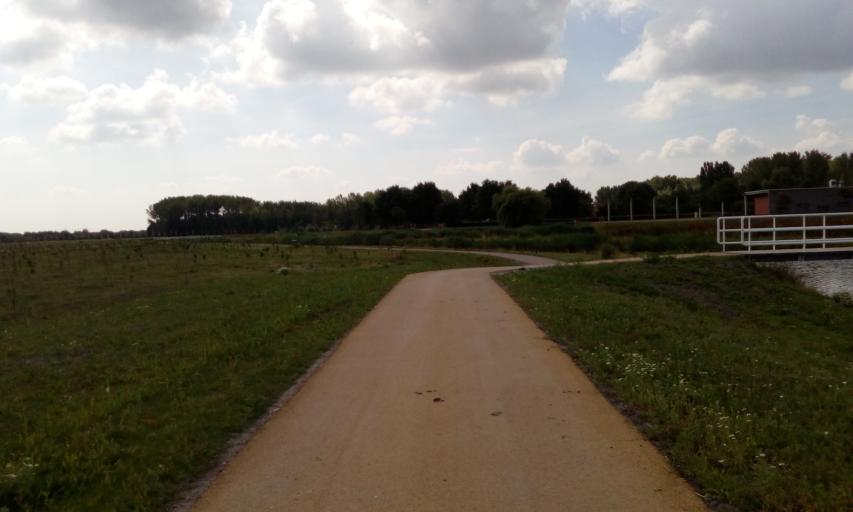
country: NL
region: South Holland
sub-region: Gemeente Pijnacker-Nootdorp
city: Pijnacker
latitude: 52.0371
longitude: 4.4130
